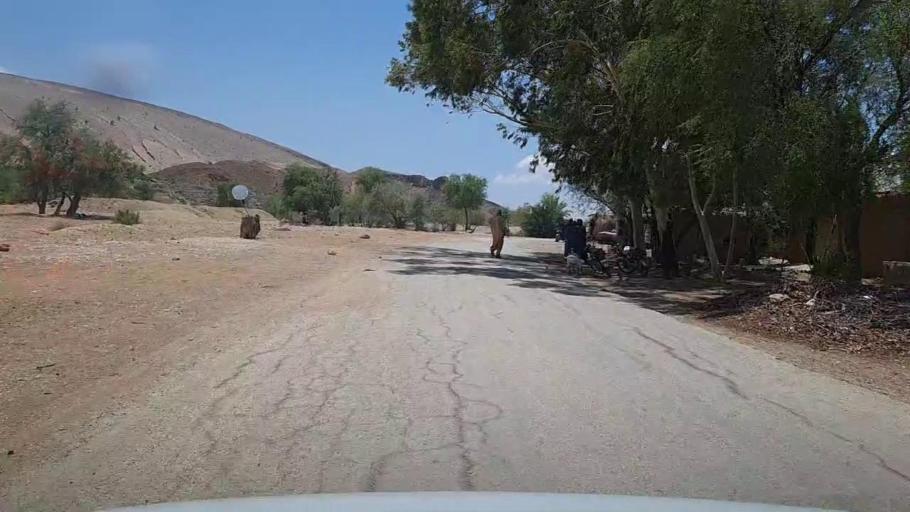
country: PK
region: Sindh
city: Bhan
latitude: 26.3025
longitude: 67.5362
